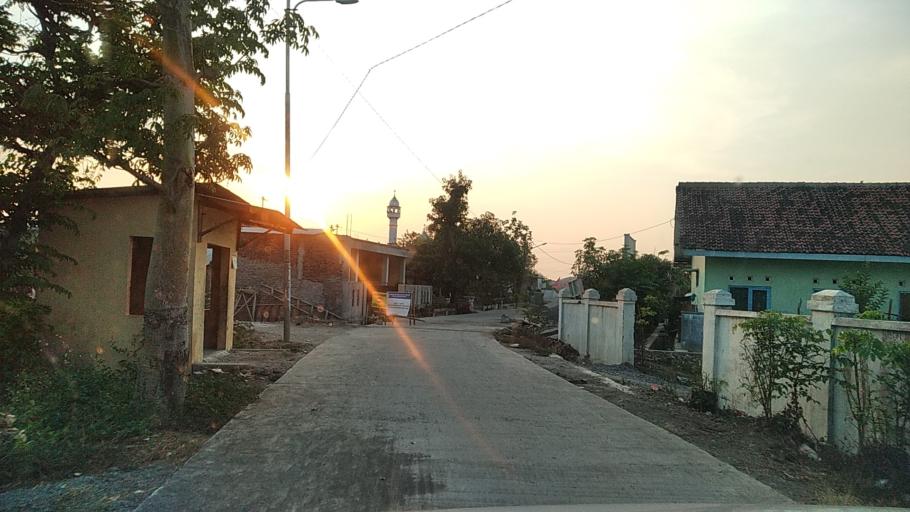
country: ID
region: Central Java
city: Semarang
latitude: -6.9588
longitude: 110.3044
